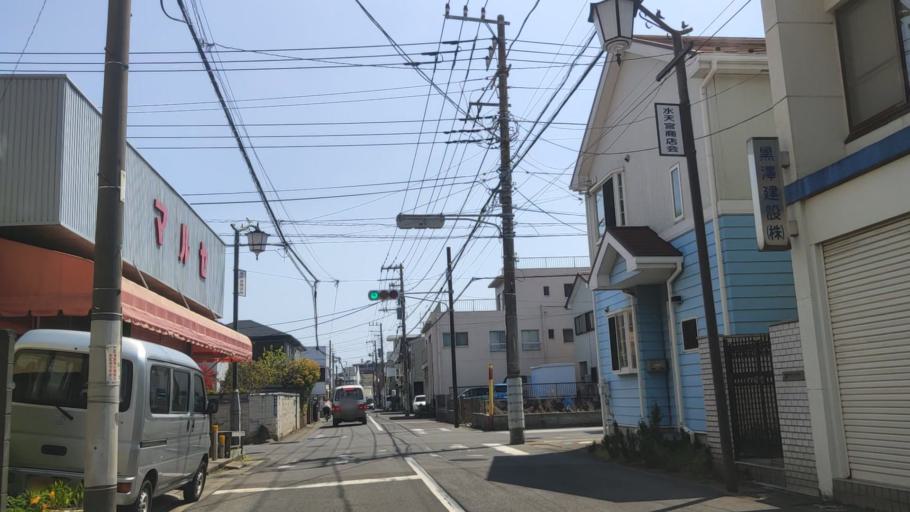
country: JP
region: Kanagawa
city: Hiratsuka
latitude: 35.3365
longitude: 139.3336
